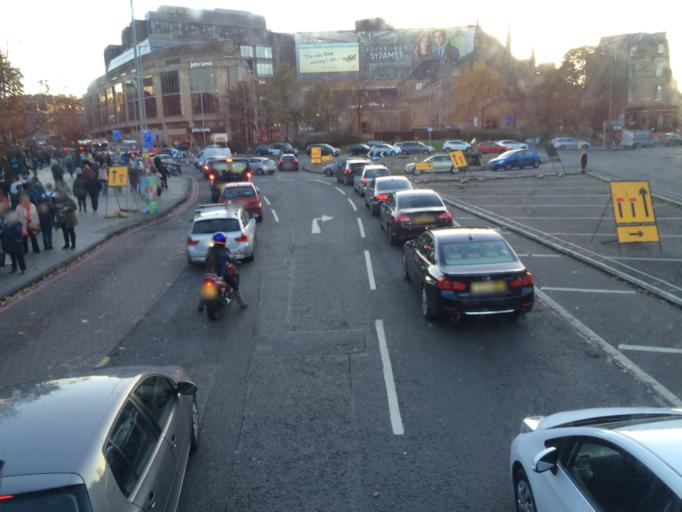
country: GB
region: Scotland
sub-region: Edinburgh
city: Edinburgh
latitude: 55.9569
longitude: -3.1859
